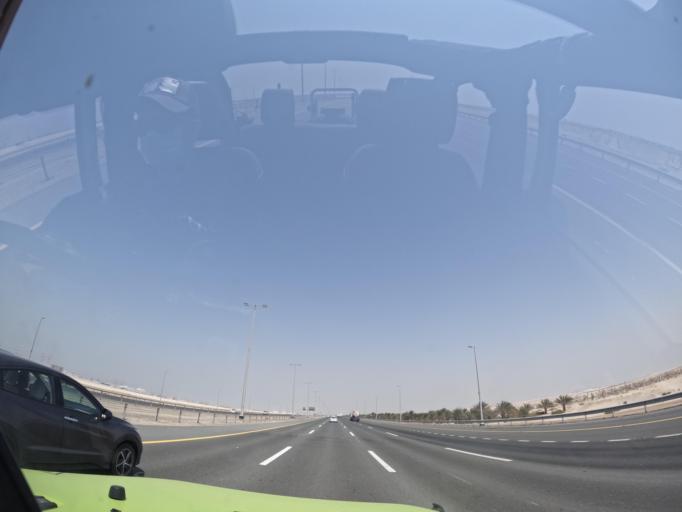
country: AE
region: Abu Dhabi
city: Abu Dhabi
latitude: 24.2529
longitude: 54.4801
